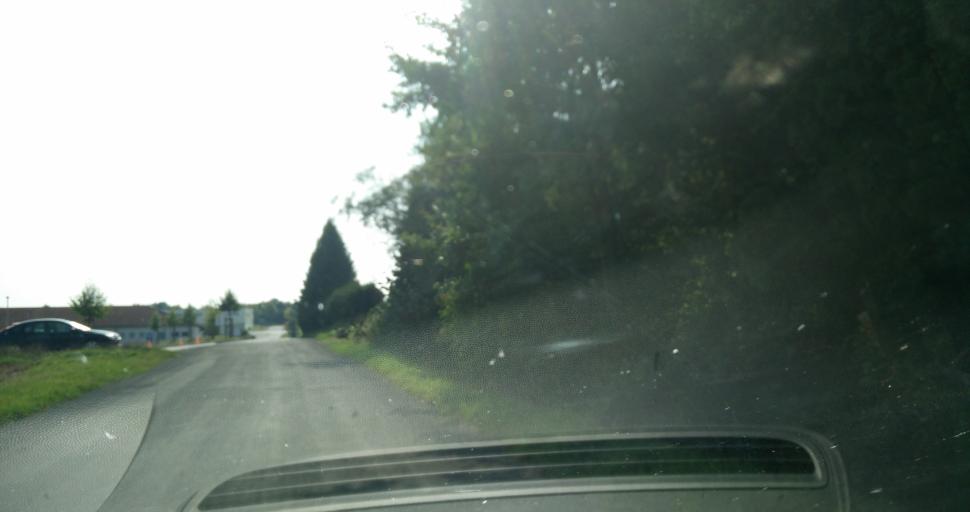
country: DE
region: Saxony
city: Colditz
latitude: 51.1397
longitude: 12.7918
